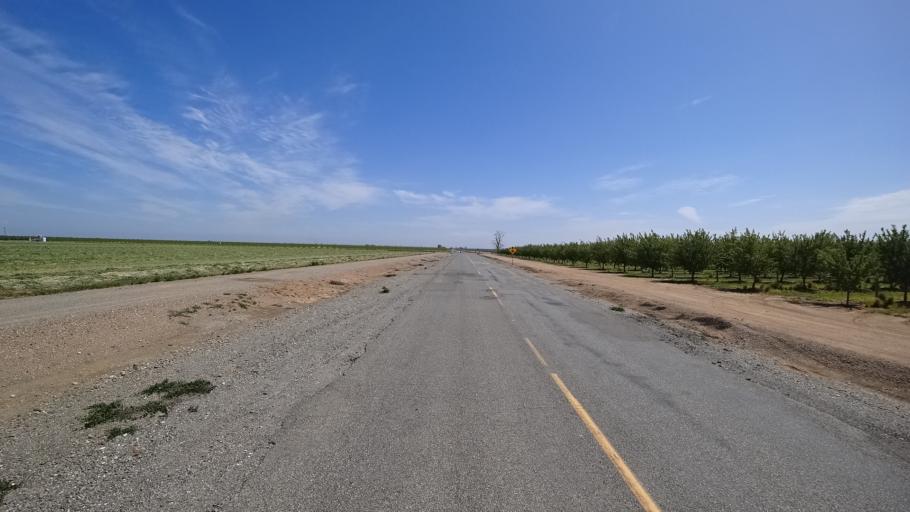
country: US
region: California
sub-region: Glenn County
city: Orland
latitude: 39.6527
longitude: -122.1433
